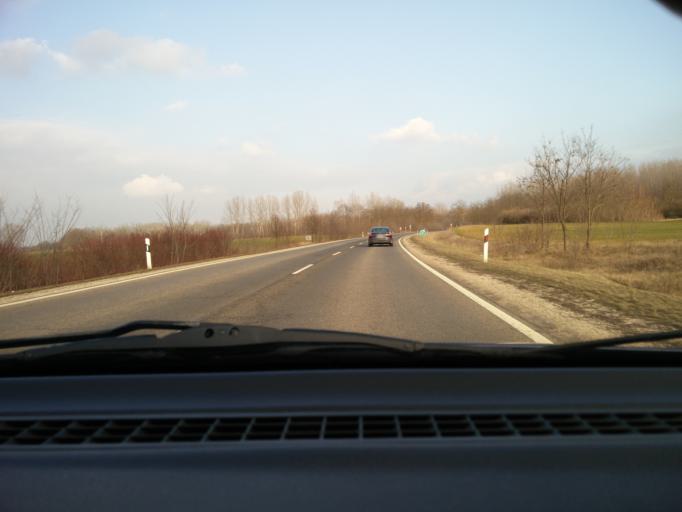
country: HU
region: Pest
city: Nyaregyhaza
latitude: 47.2484
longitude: 19.4542
